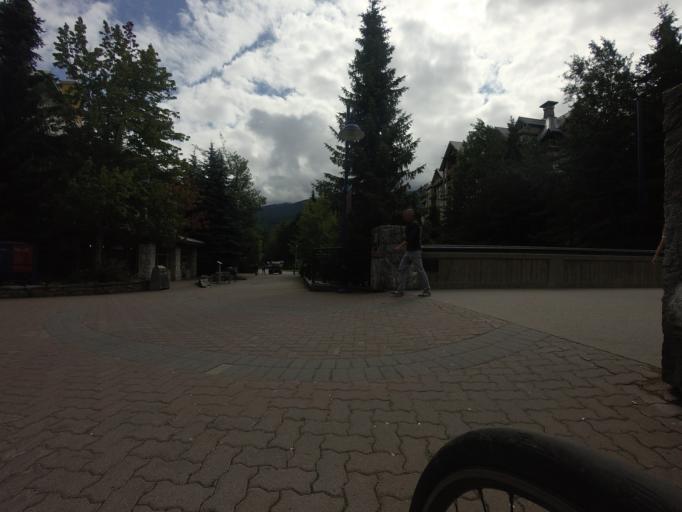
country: CA
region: British Columbia
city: Whistler
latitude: 50.1162
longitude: -122.9553
